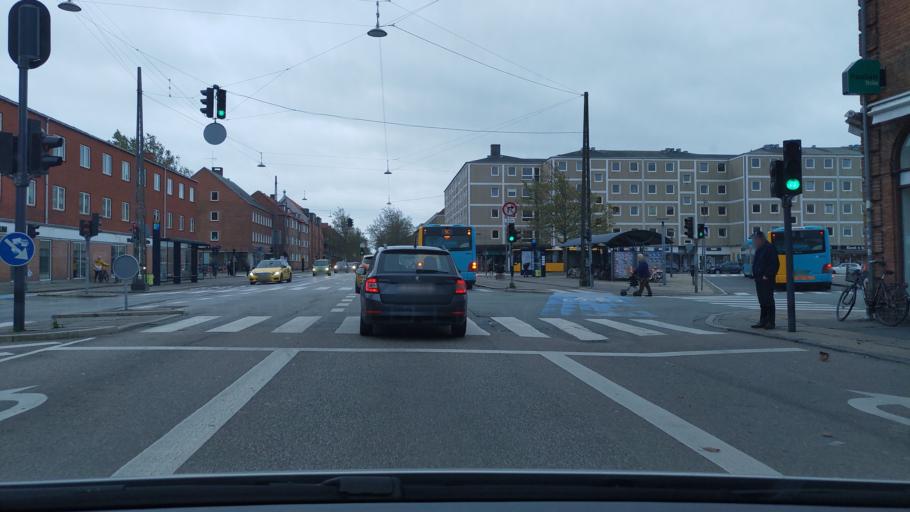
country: DK
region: Capital Region
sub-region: Tarnby Kommune
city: Tarnby
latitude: 55.6470
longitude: 12.6140
